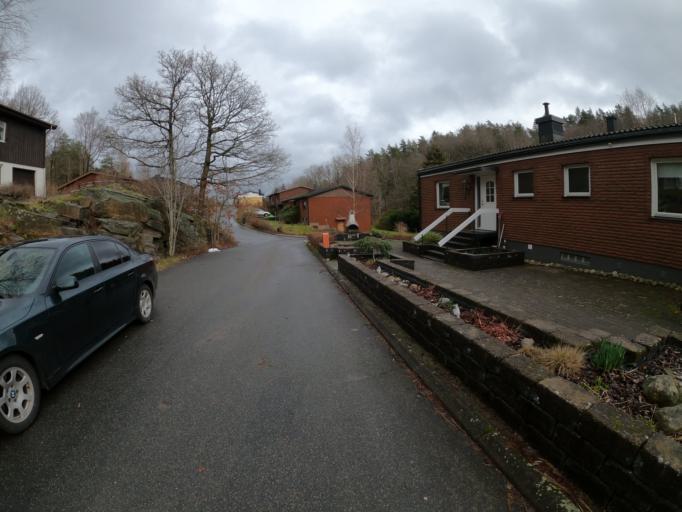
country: SE
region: Vaestra Goetaland
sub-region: Harryda Kommun
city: Molnlycke
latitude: 57.6445
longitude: 12.1149
